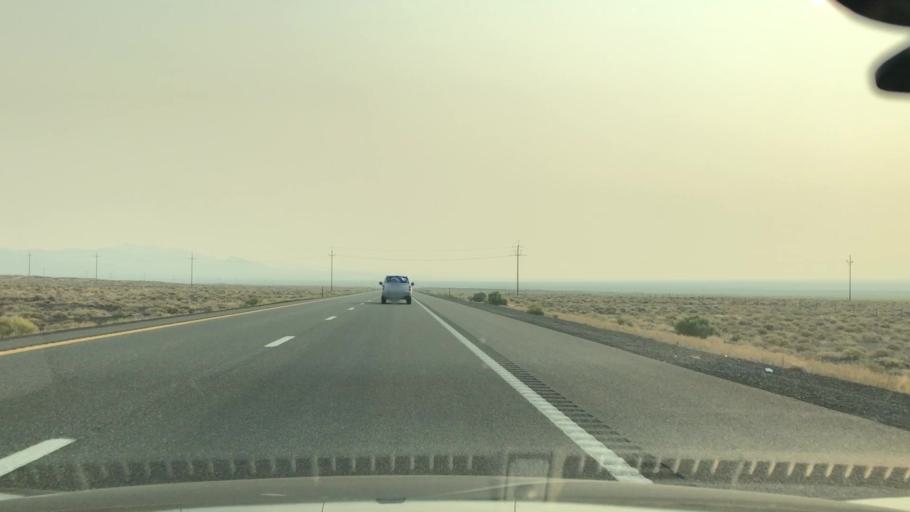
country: US
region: Nevada
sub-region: Churchill County
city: Fallon
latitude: 39.8924
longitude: -118.8527
